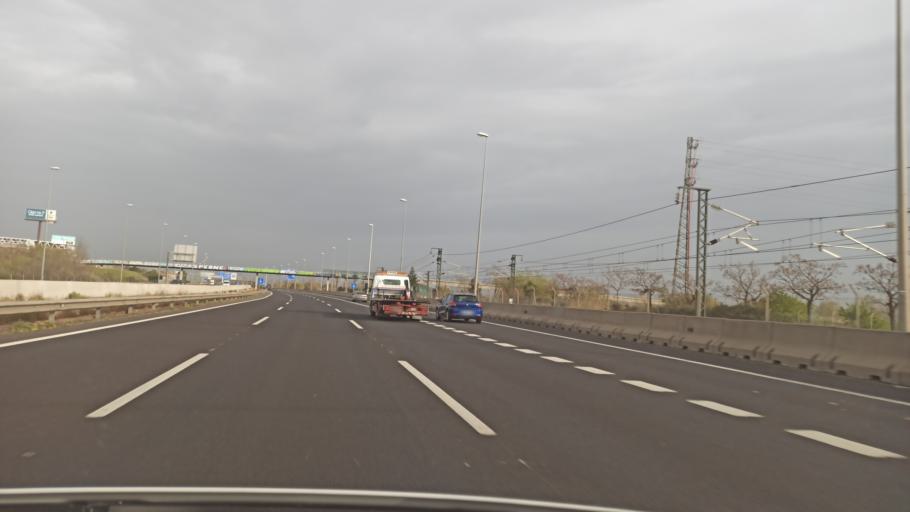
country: ES
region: Catalonia
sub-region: Provincia de Barcelona
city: Cornella de Llobregat
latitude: 41.3478
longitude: 2.0658
